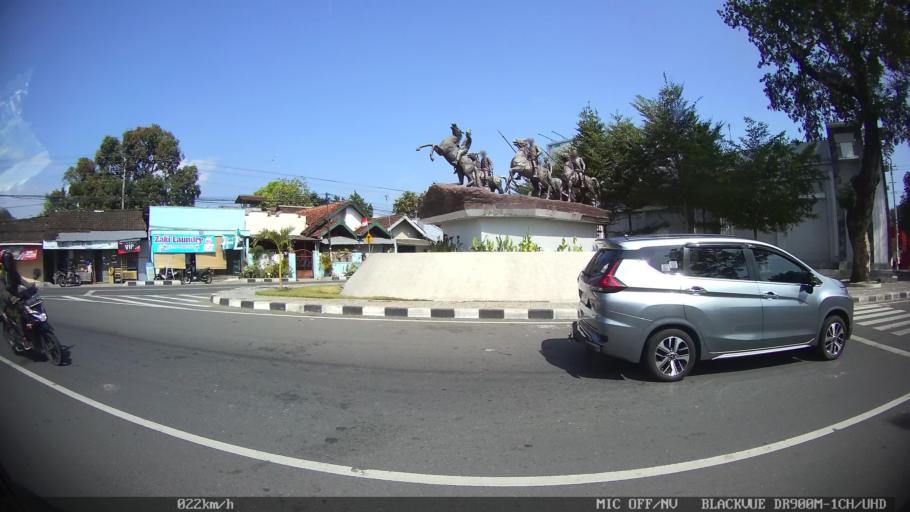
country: ID
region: Daerah Istimewa Yogyakarta
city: Pundong
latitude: -7.9198
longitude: 110.3814
